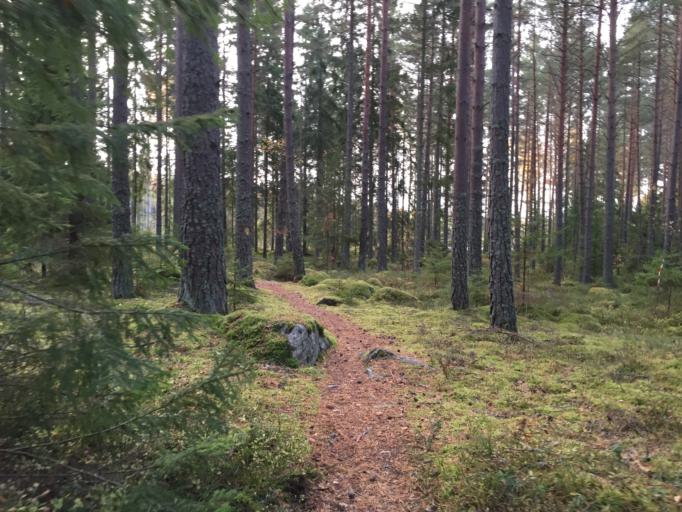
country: SE
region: Vaestmanland
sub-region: Hallstahammars Kommun
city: Hallstahammar
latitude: 59.6310
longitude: 16.2472
